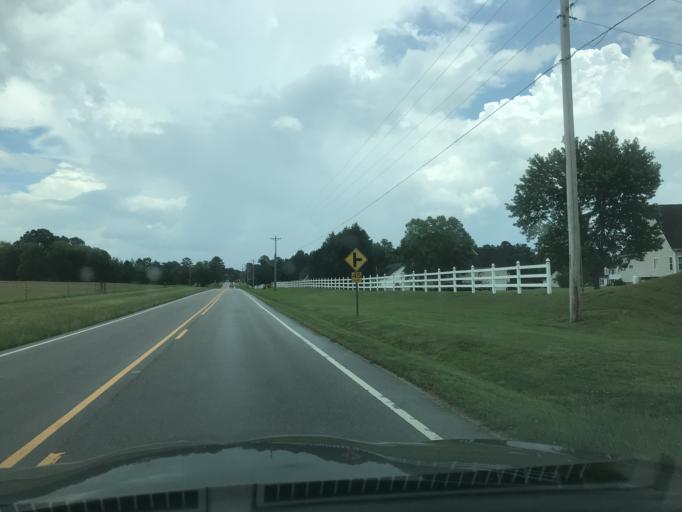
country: US
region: North Carolina
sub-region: Wake County
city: Knightdale
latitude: 35.8380
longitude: -78.4962
